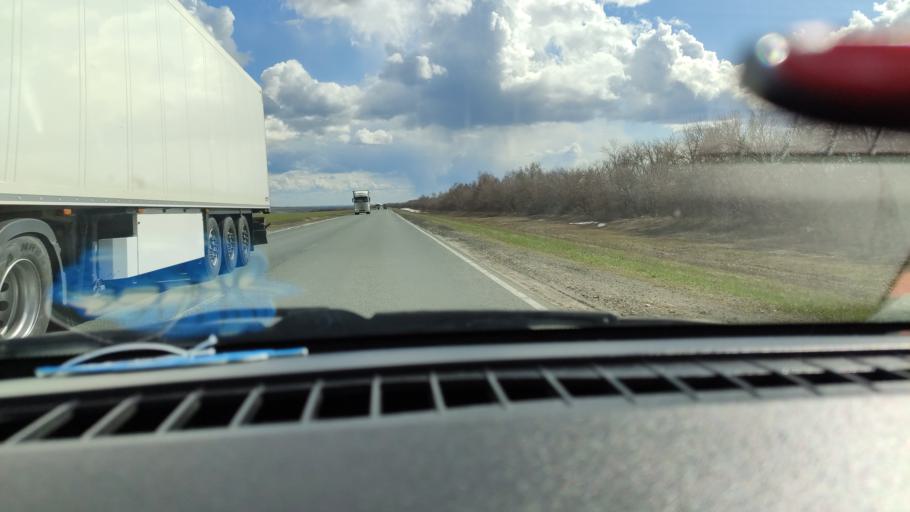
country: RU
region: Saratov
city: Dukhovnitskoye
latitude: 52.7711
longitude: 48.2362
